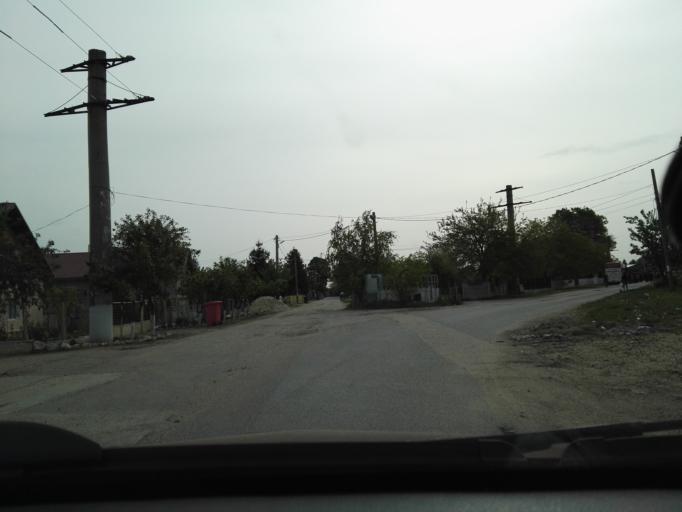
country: RO
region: Giurgiu
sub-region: Comuna Mihailesti
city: Mihailesti
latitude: 44.3428
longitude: 25.8840
